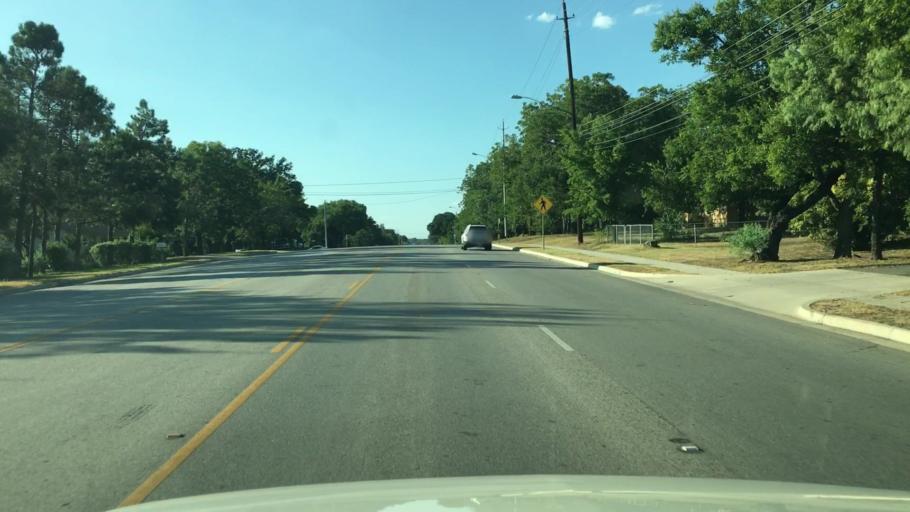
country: US
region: Texas
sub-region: Burnet County
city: Burnet
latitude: 30.7700
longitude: -98.2317
